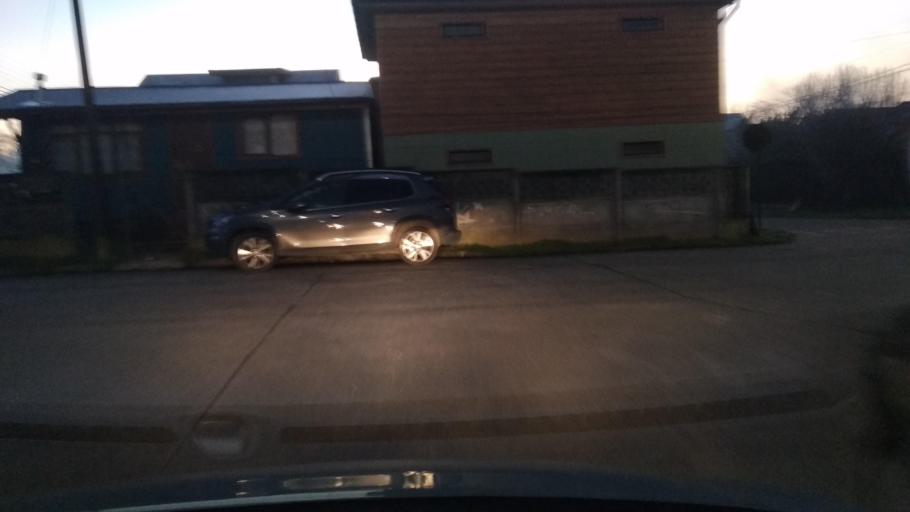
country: CL
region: Los Rios
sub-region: Provincia de Valdivia
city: Valdivia
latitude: -39.8138
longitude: -73.2575
